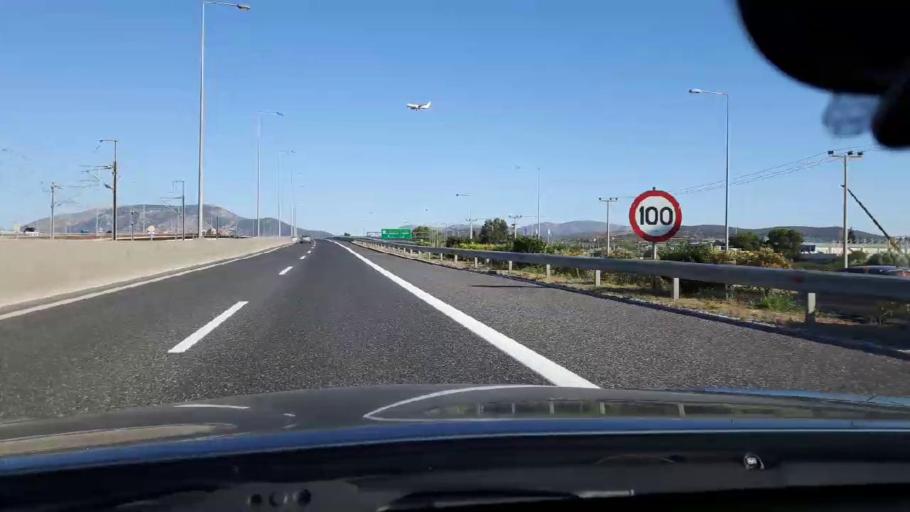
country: GR
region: Attica
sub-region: Nomarchia Anatolikis Attikis
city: Koropi
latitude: 37.9013
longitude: 23.9051
